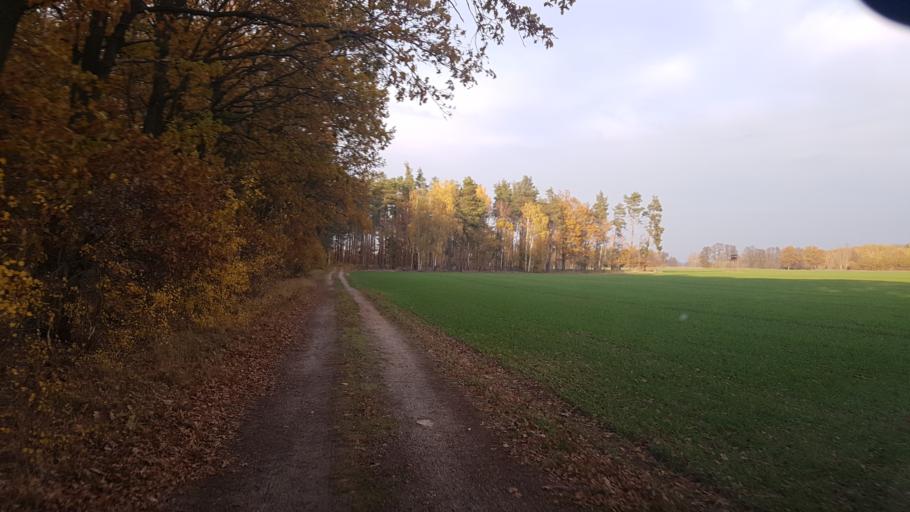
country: DE
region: Brandenburg
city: Schonewalde
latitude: 51.6402
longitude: 13.5997
